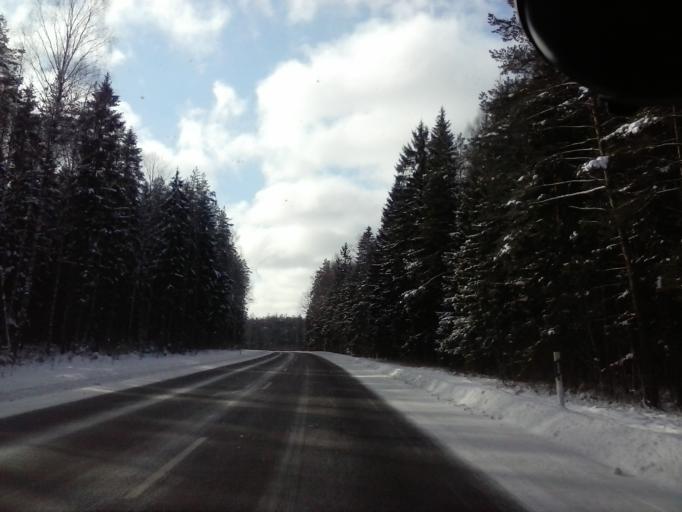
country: EE
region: Viljandimaa
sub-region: Moisakuela linn
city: Moisakula
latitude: 58.2426
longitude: 25.1307
